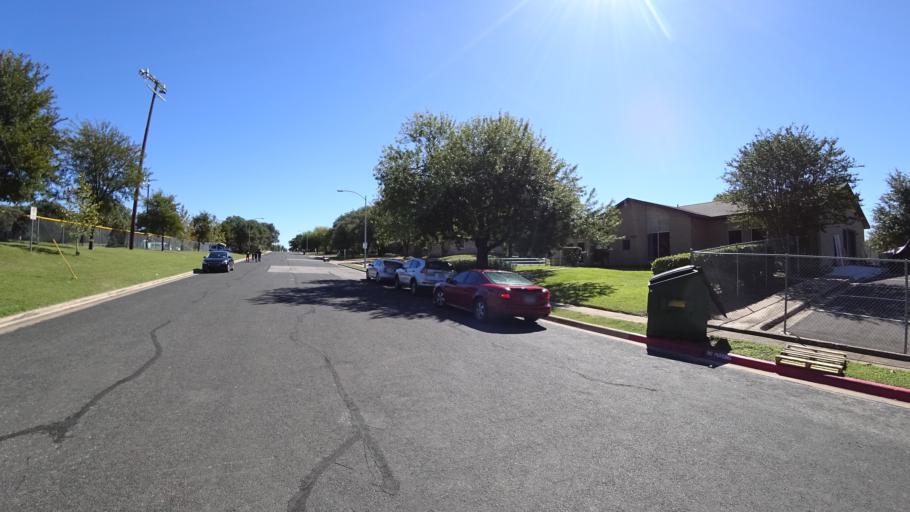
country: US
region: Texas
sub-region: Travis County
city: Austin
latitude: 30.2416
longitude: -97.7703
